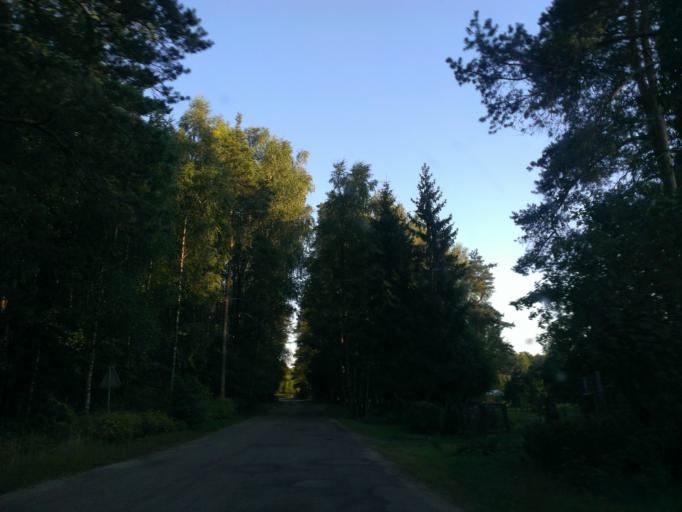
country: LV
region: Garkalne
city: Garkalne
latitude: 57.0503
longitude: 24.4360
